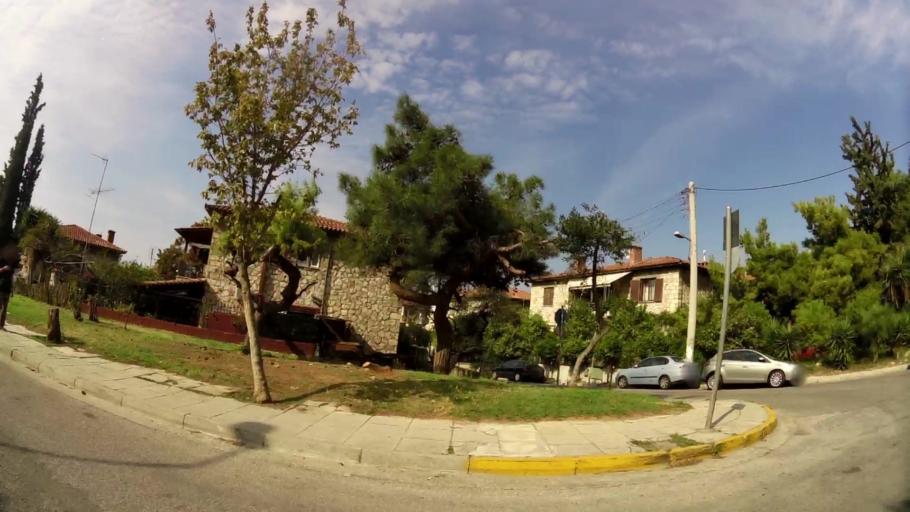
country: GR
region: Attica
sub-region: Nomarchia Athinas
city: Athens
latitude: 37.9719
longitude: 23.7164
